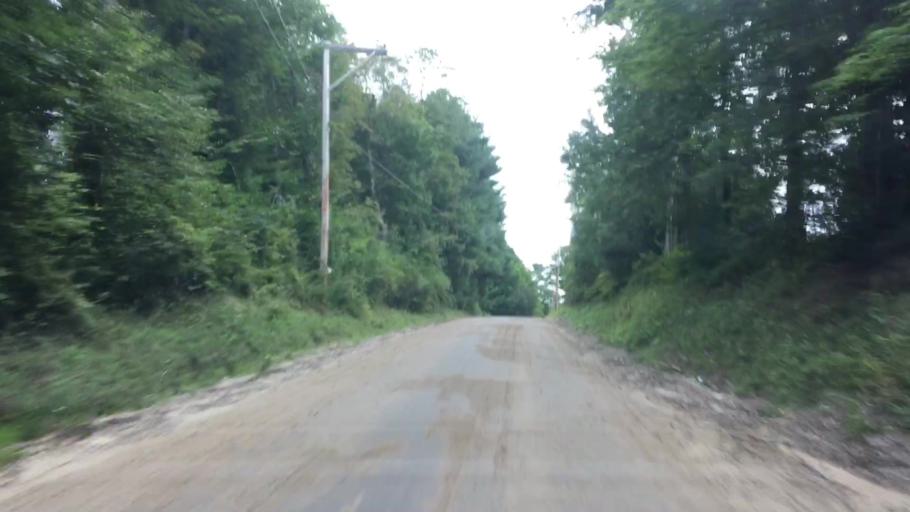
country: US
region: Maine
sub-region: Cumberland County
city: New Gloucester
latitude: 43.9065
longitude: -70.2348
